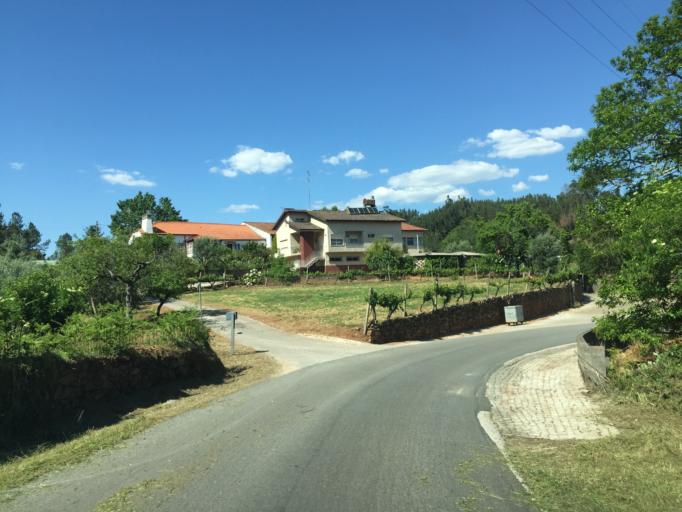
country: PT
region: Leiria
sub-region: Alvaiazere
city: Alvaiazere
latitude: 39.8431
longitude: -8.3775
